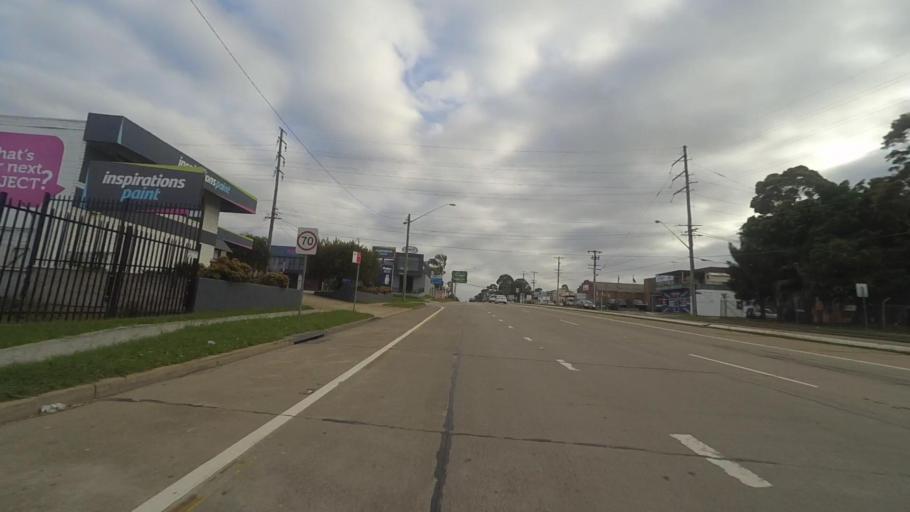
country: AU
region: New South Wales
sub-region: Bankstown
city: Padstow
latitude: -33.9372
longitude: 151.0364
